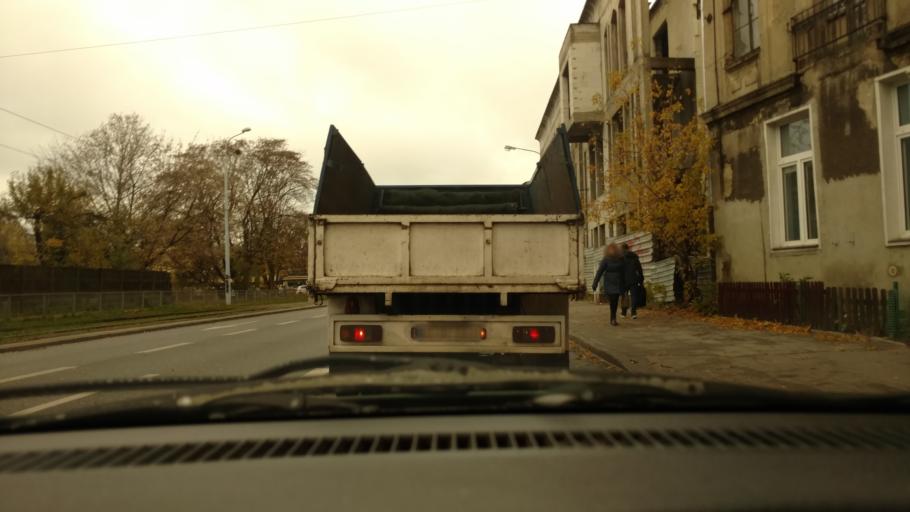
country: PL
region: Lodz Voivodeship
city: Lodz
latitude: 51.7778
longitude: 19.4935
